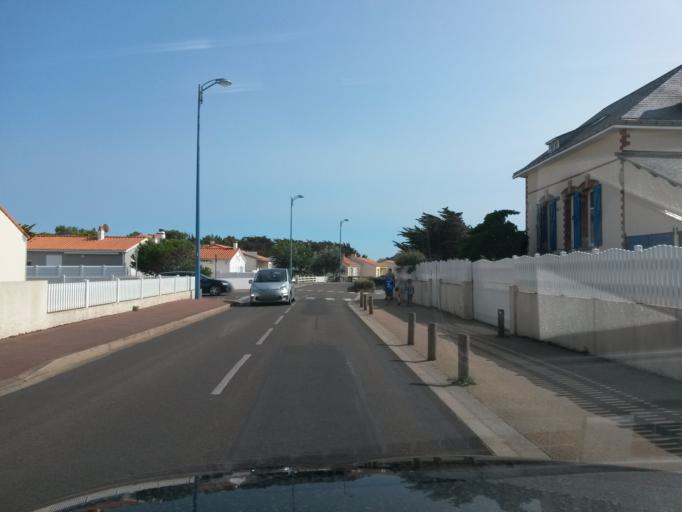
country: FR
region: Pays de la Loire
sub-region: Departement de la Vendee
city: Bretignolles-sur-Mer
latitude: 46.6221
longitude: -1.8725
